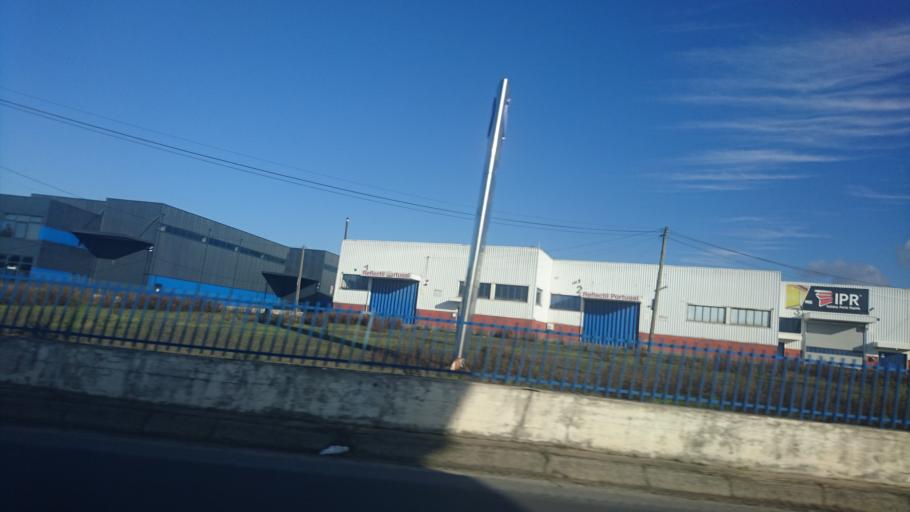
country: PT
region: Porto
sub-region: Valongo
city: Campo
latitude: 41.1724
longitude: -8.4412
